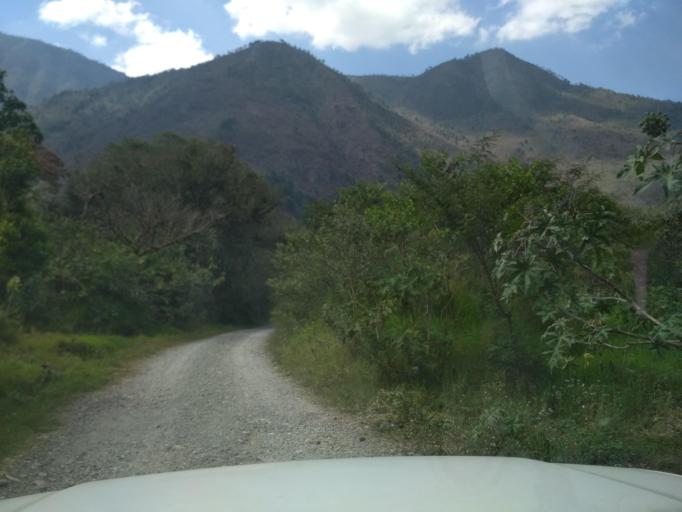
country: MX
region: Veracruz
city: Jalapilla
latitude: 18.7985
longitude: -97.1031
